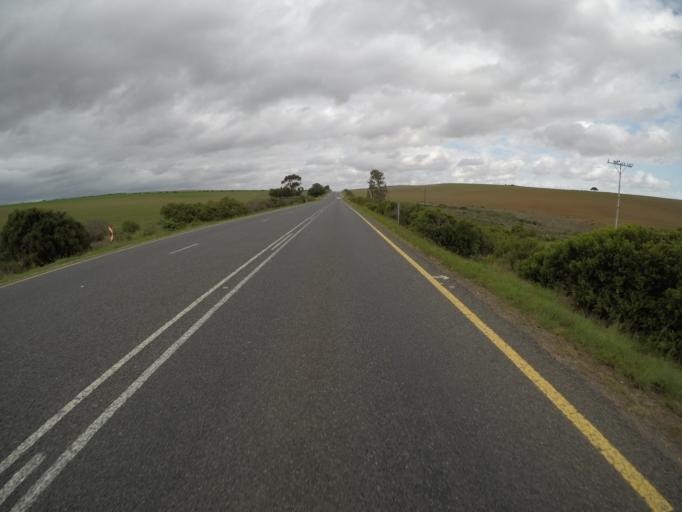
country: ZA
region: Western Cape
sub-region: Eden District Municipality
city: Riversdale
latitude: -34.1172
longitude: 20.8596
